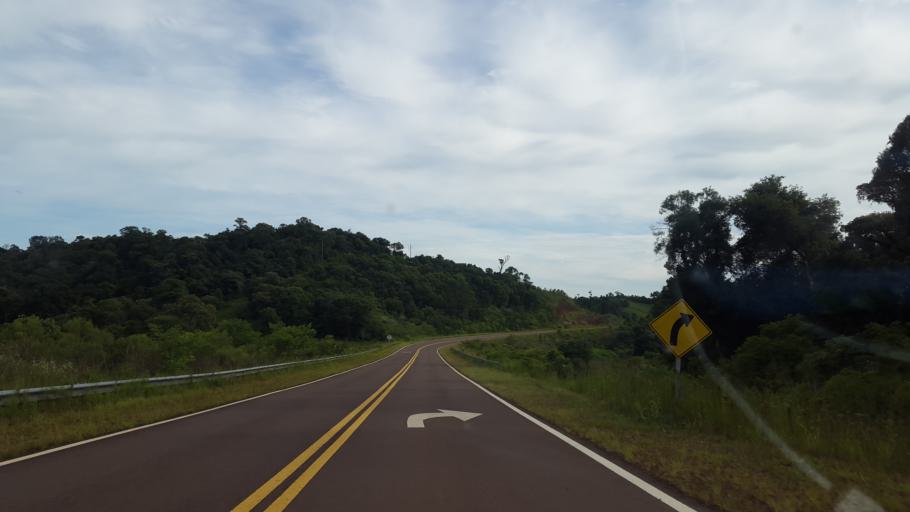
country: AR
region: Misiones
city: Bernardo de Irigoyen
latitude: -26.4060
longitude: -53.8217
